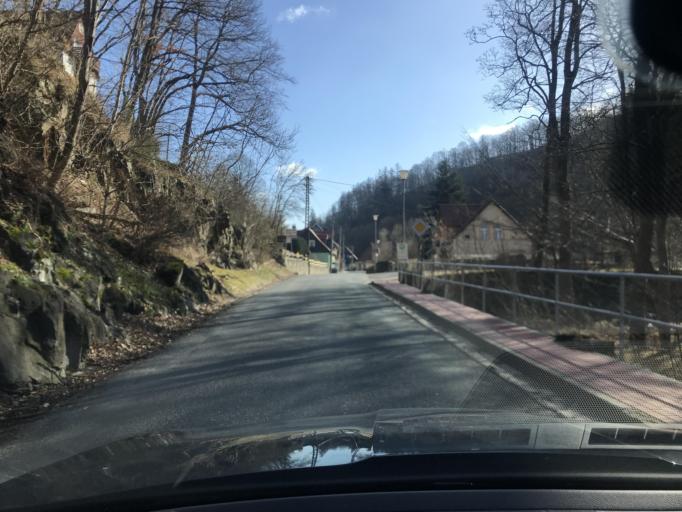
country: DE
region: Saxony-Anhalt
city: Huttenrode
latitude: 51.7276
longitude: 10.9316
